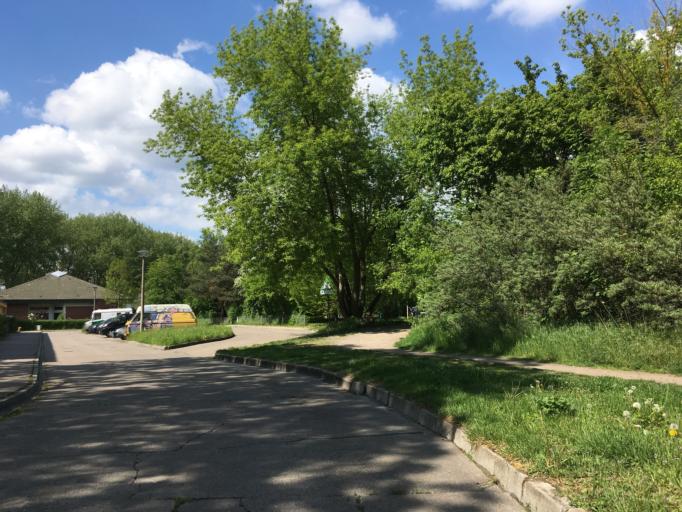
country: DE
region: Berlin
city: Neu-Hohenschoenhausen
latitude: 52.5739
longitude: 13.4999
